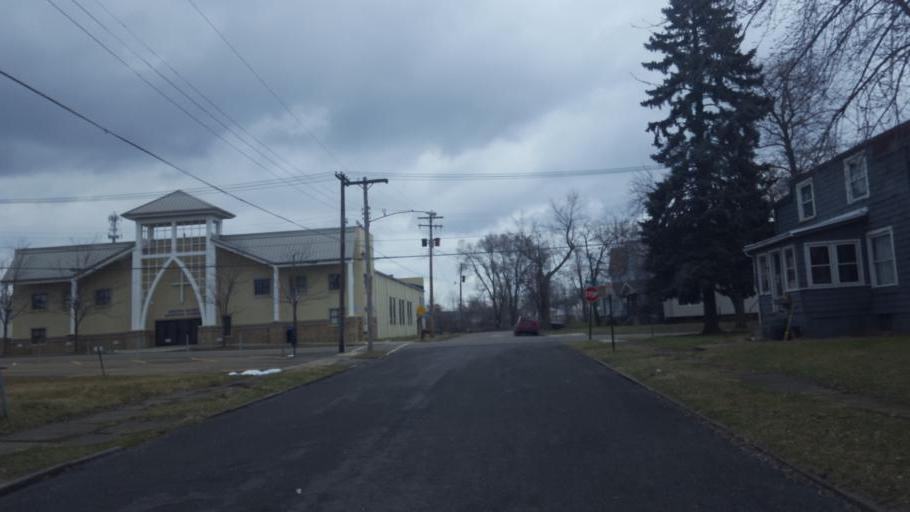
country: US
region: Ohio
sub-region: Stark County
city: Canton
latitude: 40.7833
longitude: -81.4010
